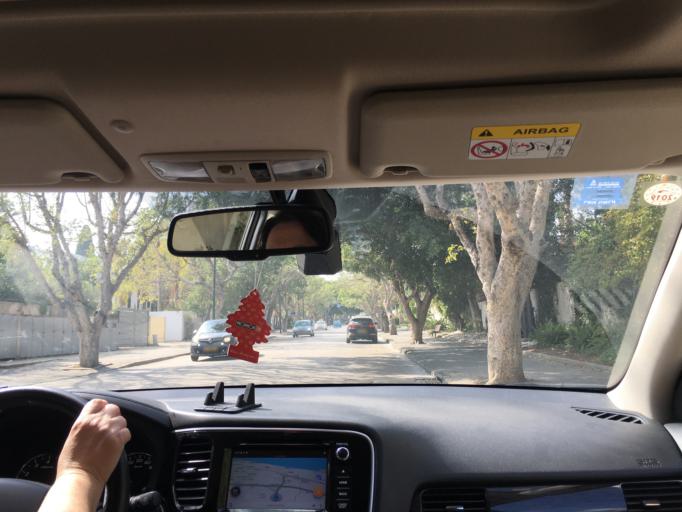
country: IL
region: Tel Aviv
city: Kefar Shemaryahu
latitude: 32.1805
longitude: 34.8134
